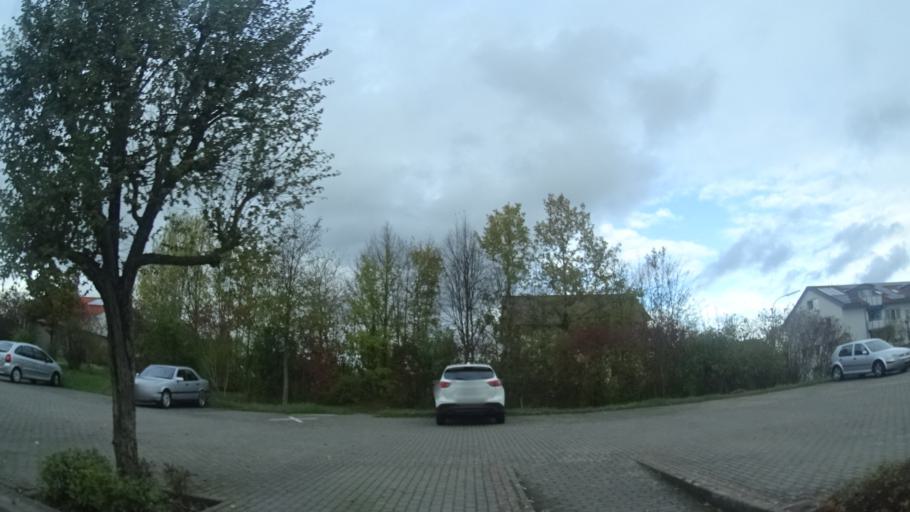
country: DE
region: Bavaria
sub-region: Regierungsbezirk Unterfranken
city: Bad Neustadt an der Saale
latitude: 50.3298
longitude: 10.2061
